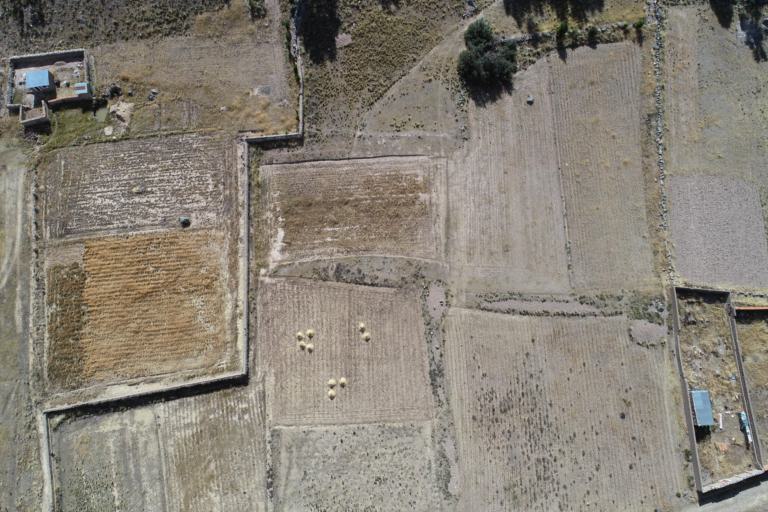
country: BO
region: La Paz
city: Achacachi
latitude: -15.8940
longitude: -68.9083
